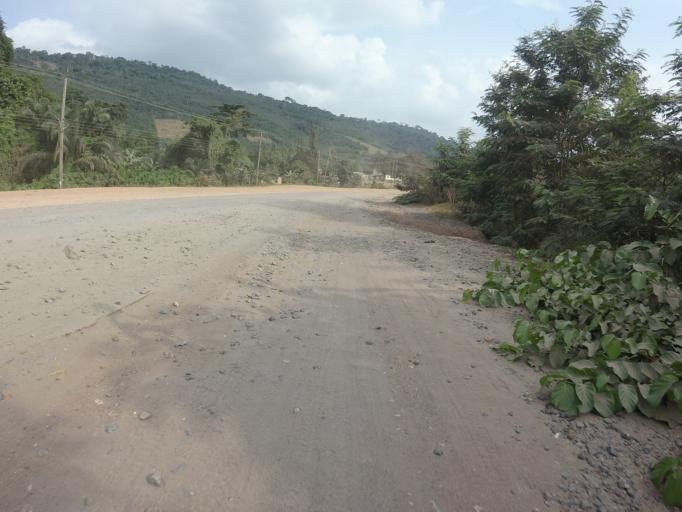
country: GH
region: Volta
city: Ho
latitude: 6.6282
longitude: 0.3115
